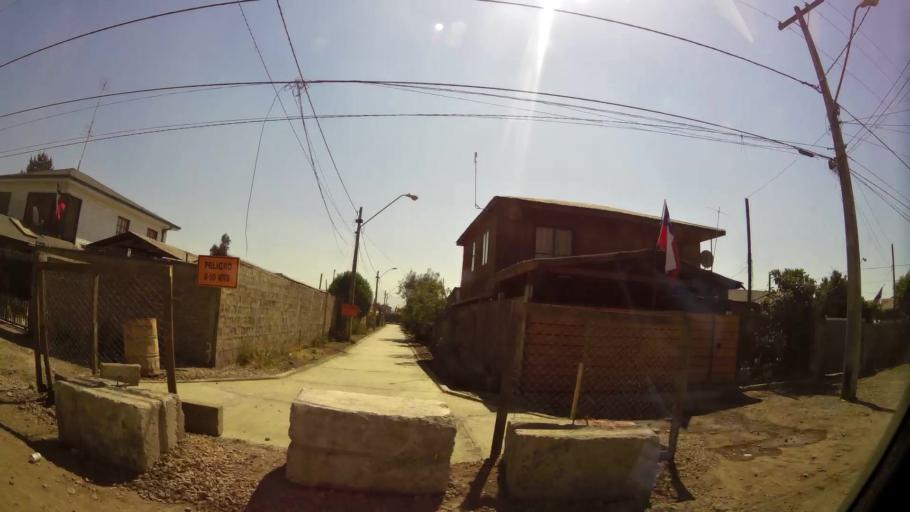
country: CL
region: Santiago Metropolitan
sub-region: Provincia de Talagante
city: Penaflor
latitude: -33.5801
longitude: -70.8051
